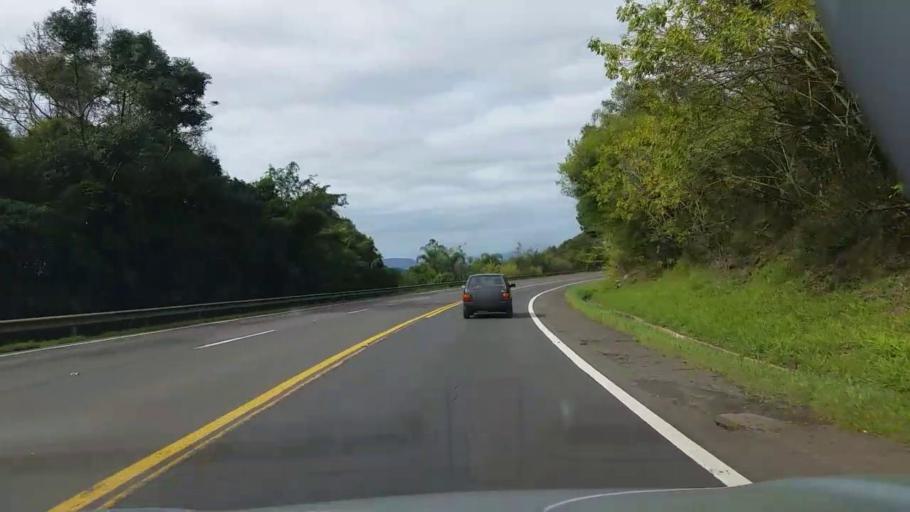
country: BR
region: Rio Grande do Sul
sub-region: Arroio Do Meio
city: Arroio do Meio
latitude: -29.3878
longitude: -52.0443
